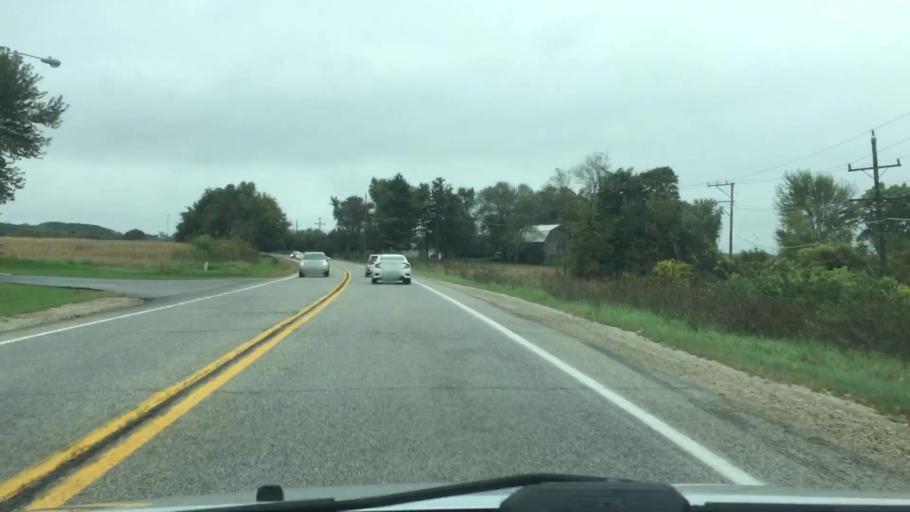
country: US
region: Illinois
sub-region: McHenry County
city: Prairie Grove
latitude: 42.3000
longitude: -88.2865
